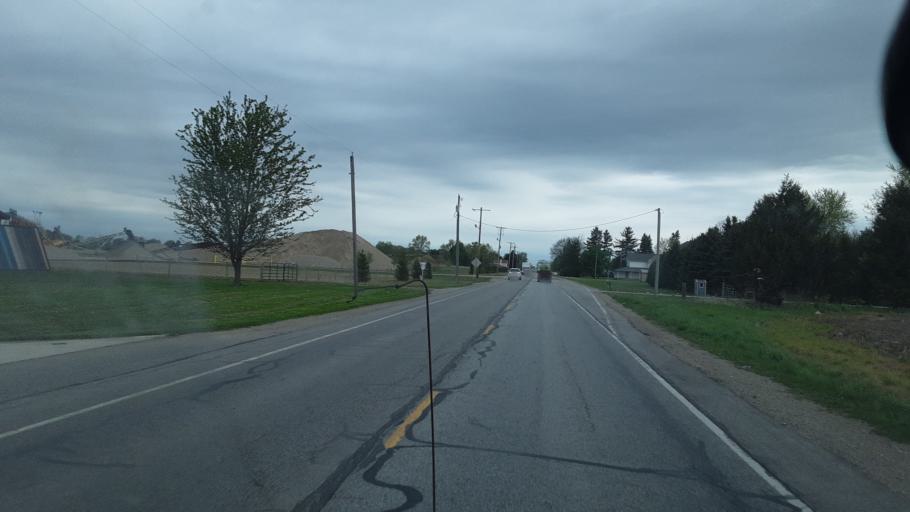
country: US
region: Indiana
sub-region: Elkhart County
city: New Paris
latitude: 41.5285
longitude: -85.7798
